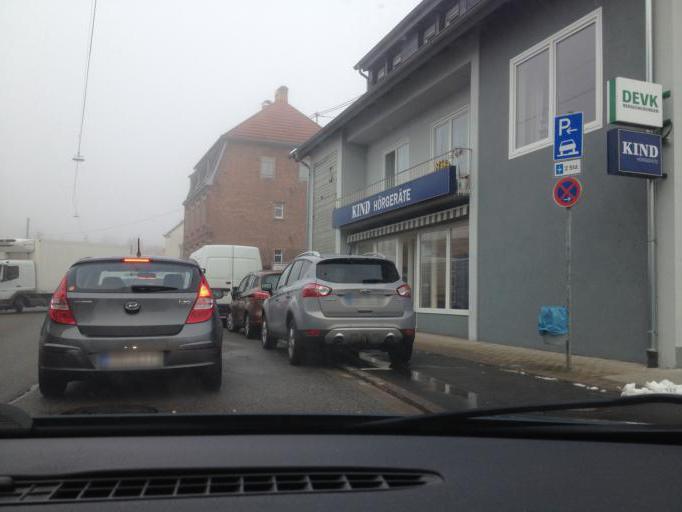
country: DE
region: Saarland
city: Sankt Wendel
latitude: 49.4697
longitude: 7.1640
